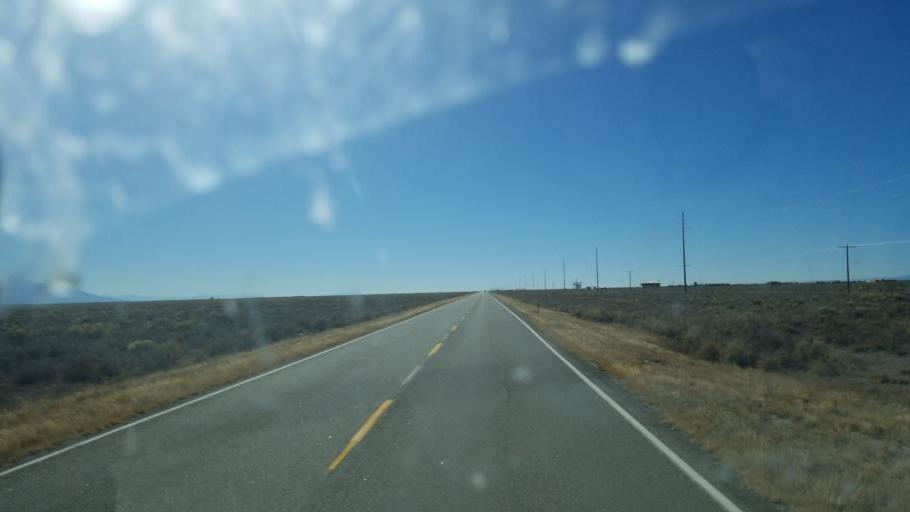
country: US
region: Colorado
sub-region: Saguache County
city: Saguache
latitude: 37.9772
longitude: -105.9061
